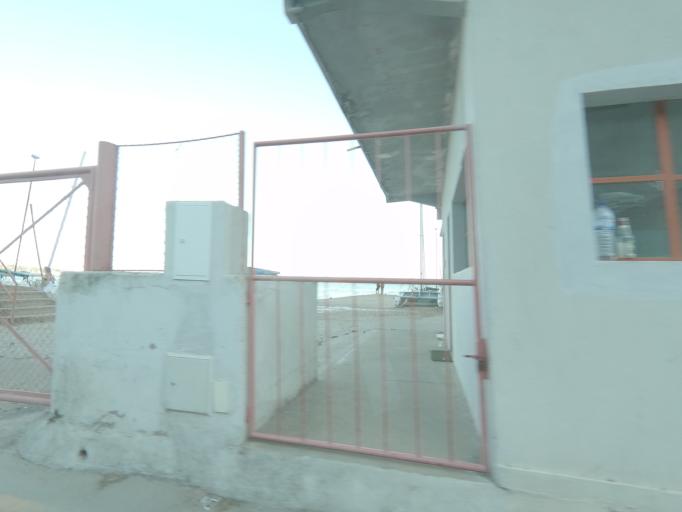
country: PT
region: Setubal
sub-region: Setubal
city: Setubal
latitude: 38.5165
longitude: -8.9073
